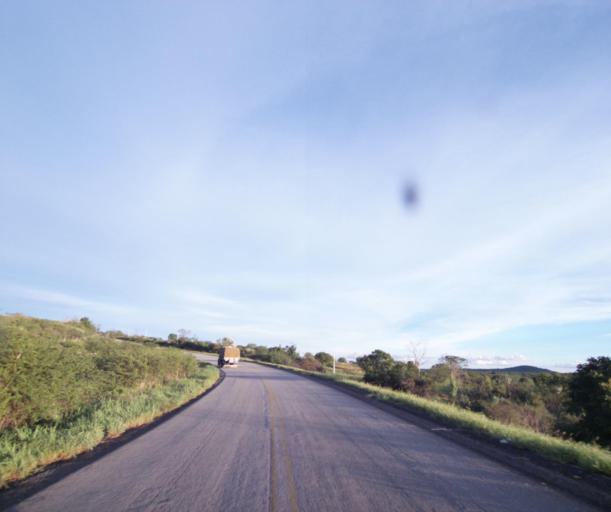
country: BR
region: Bahia
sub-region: Brumado
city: Brumado
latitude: -14.2326
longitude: -41.9173
